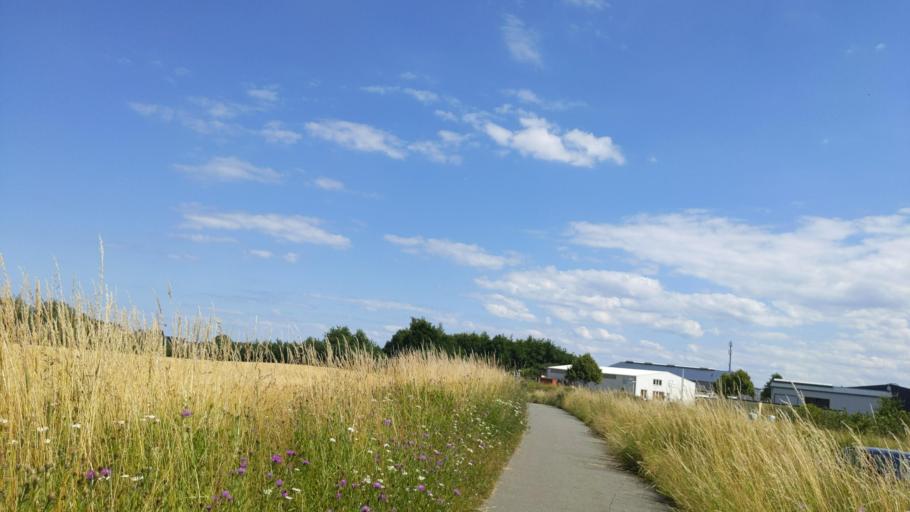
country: DE
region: Schleswig-Holstein
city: Gromitz
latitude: 54.1540
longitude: 10.9402
